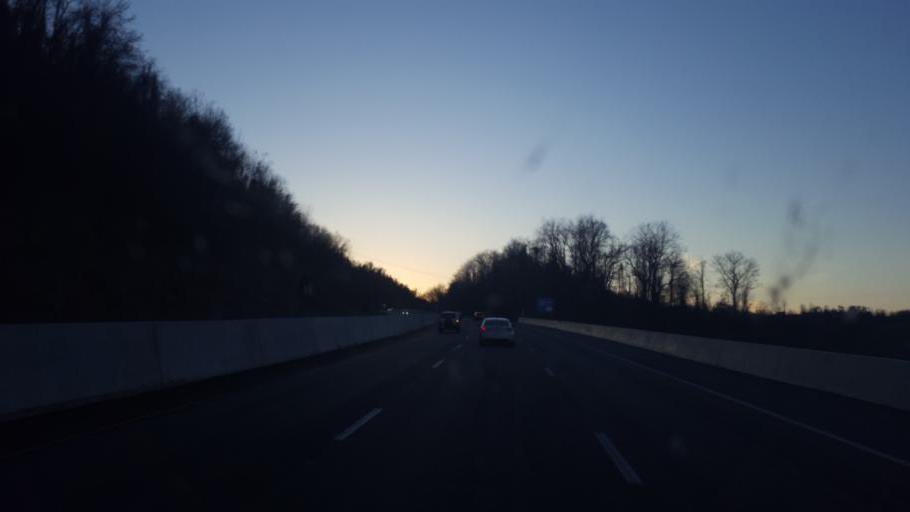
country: US
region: Ohio
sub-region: Belmont County
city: Wolfhurst
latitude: 40.0649
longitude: -80.8196
